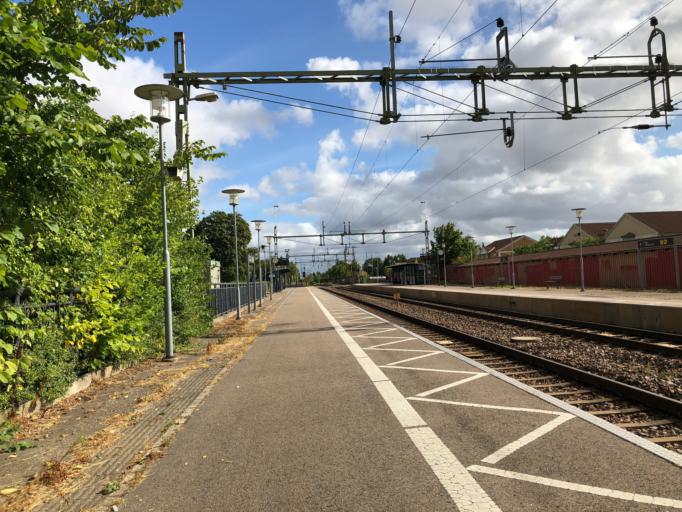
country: SE
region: Skane
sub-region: Helsingborg
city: Odakra
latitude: 56.1042
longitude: 12.7444
